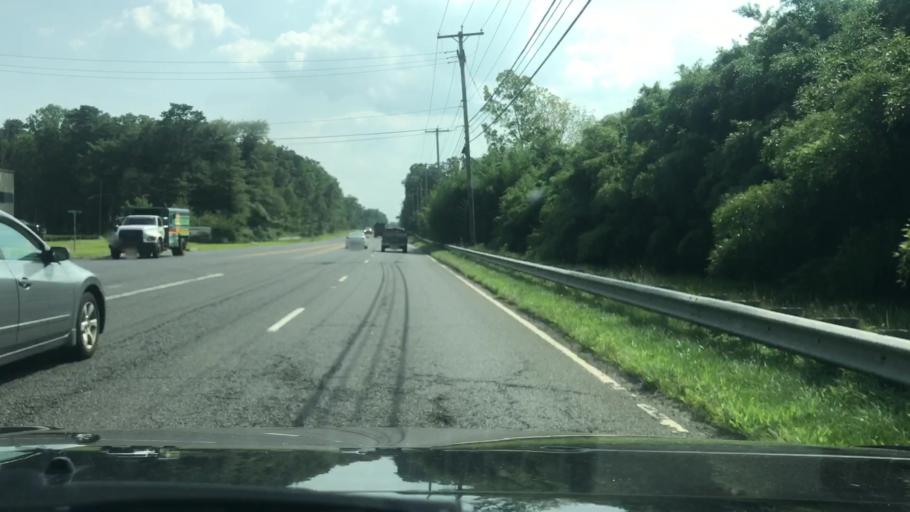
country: US
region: New Jersey
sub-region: Monmouth County
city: Tinton Falls
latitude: 40.2362
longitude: -74.1090
